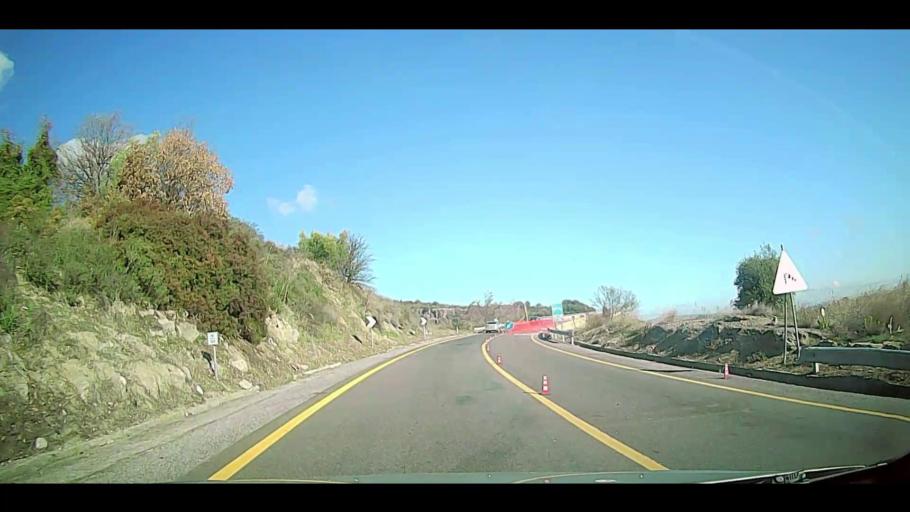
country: IT
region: Calabria
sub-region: Provincia di Crotone
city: Caccuri
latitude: 39.2222
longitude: 16.7935
